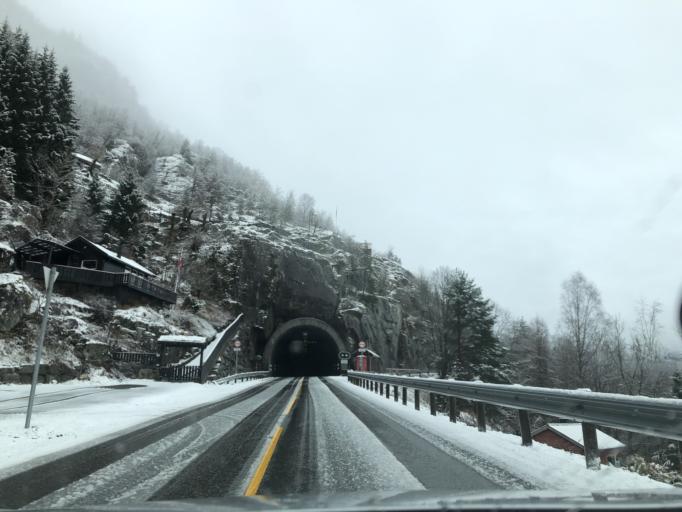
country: NO
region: Rogaland
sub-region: Sauda
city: Sauda
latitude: 59.5293
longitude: 6.5943
